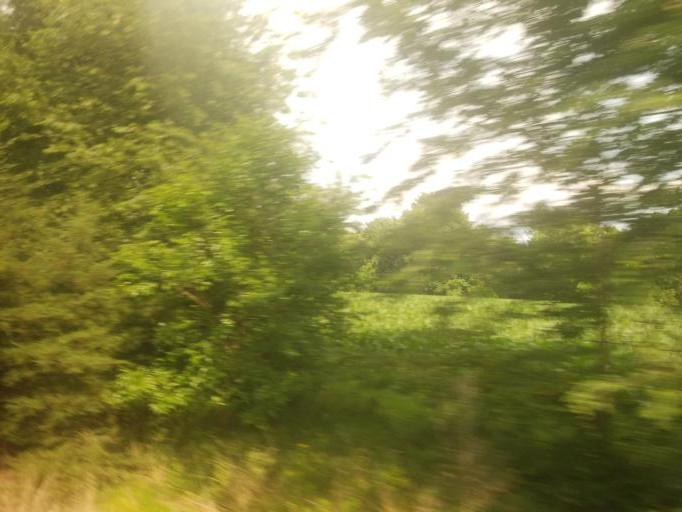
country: US
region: Illinois
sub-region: Henry County
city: Galva
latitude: 41.1156
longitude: -90.1573
